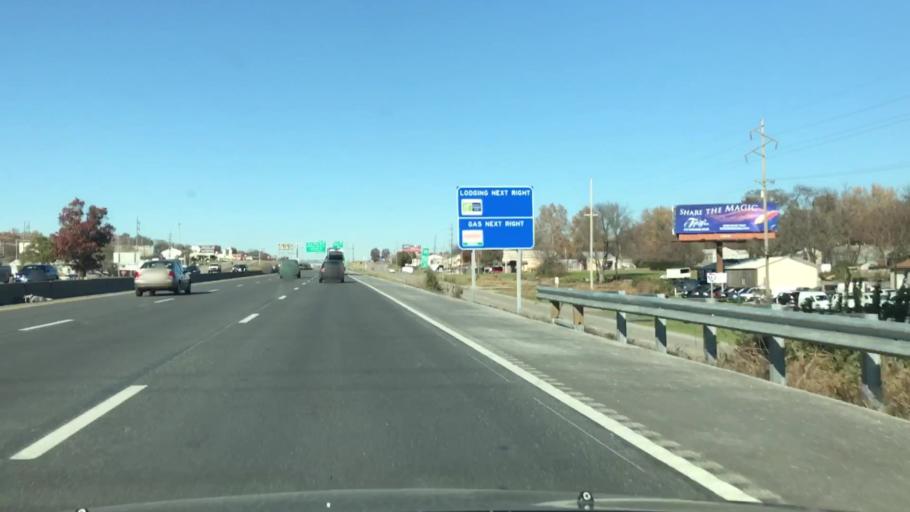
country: US
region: Missouri
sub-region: Jackson County
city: Grandview
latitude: 38.8799
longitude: -94.5257
